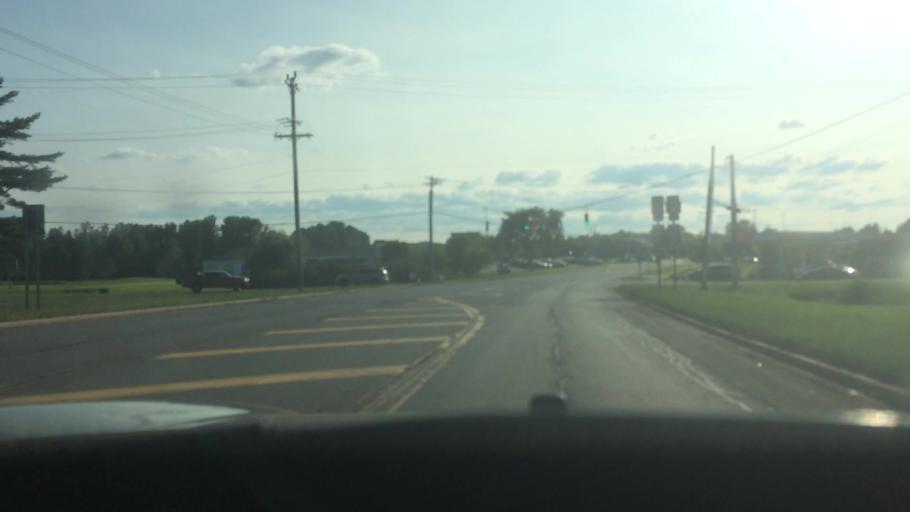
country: US
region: New York
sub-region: St. Lawrence County
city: Canton
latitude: 44.5977
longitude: -75.1466
